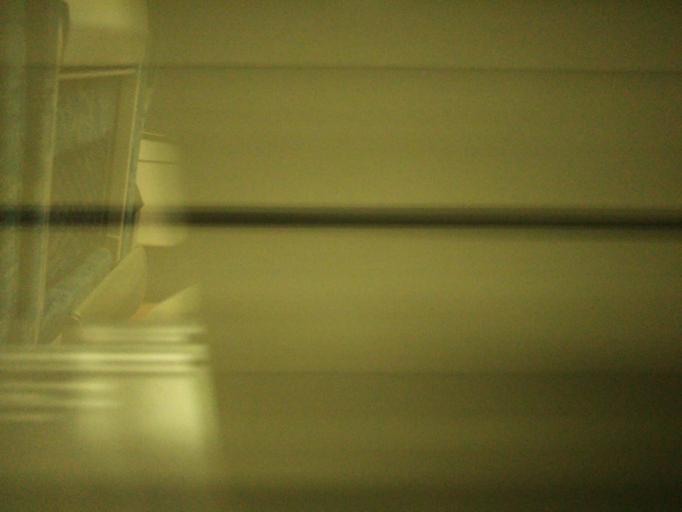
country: JP
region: Kochi
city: Nakamura
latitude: 33.0663
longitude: 133.1069
